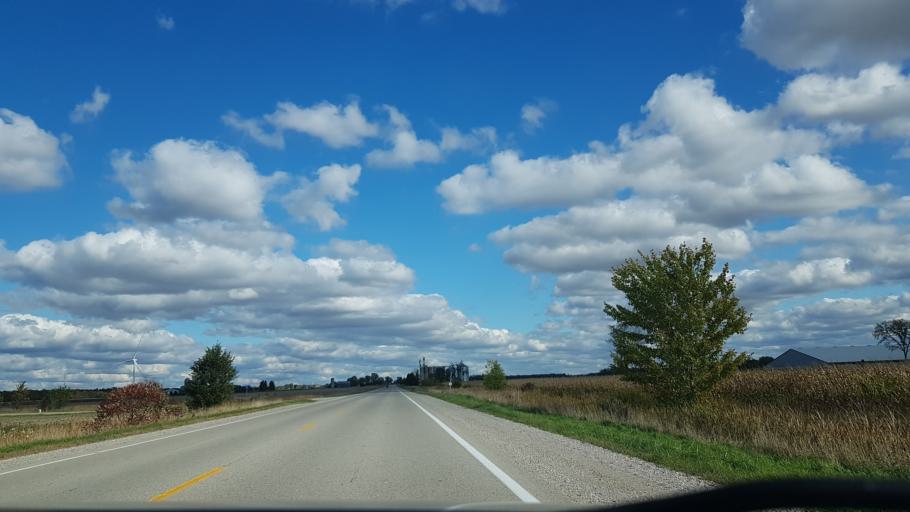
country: CA
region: Ontario
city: Lambton Shores
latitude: 43.2384
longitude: -81.7563
